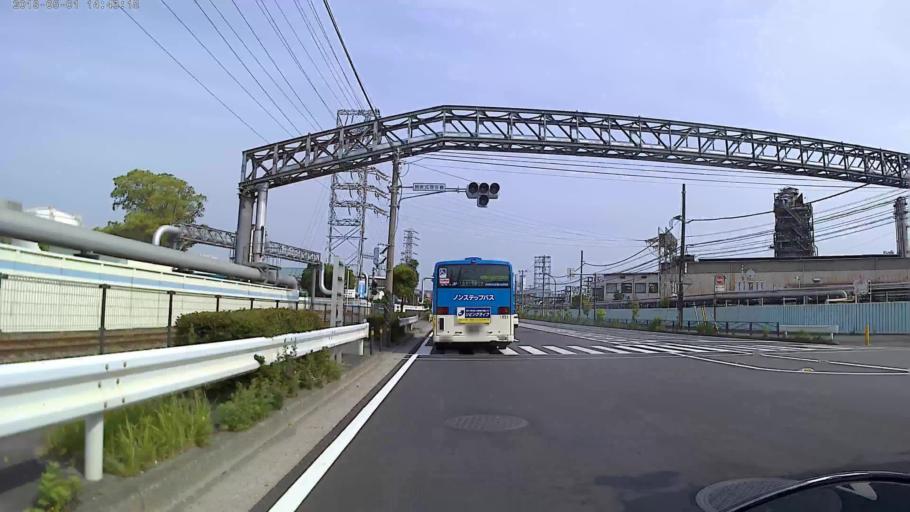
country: JP
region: Kanagawa
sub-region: Kawasaki-shi
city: Kawasaki
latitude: 35.5219
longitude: 139.7545
